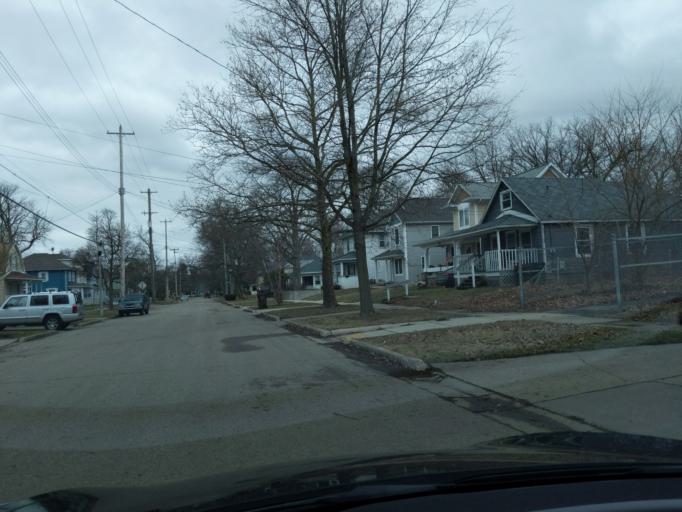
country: US
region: Michigan
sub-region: Ingham County
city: Lansing
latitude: 42.7288
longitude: -84.5697
